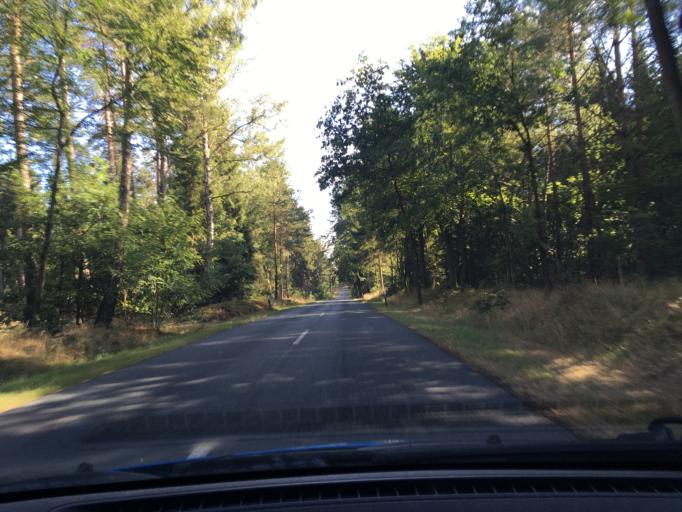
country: DE
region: Lower Saxony
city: Thomasburg
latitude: 53.2416
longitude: 10.7057
